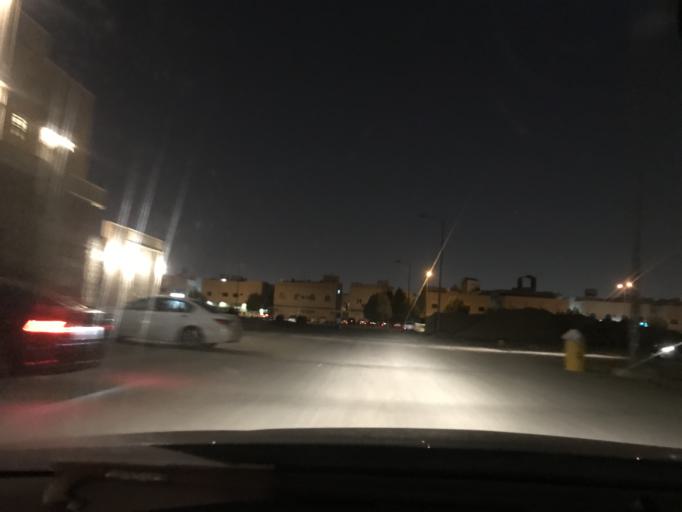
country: SA
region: Ar Riyad
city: Riyadh
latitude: 24.7487
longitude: 46.7577
